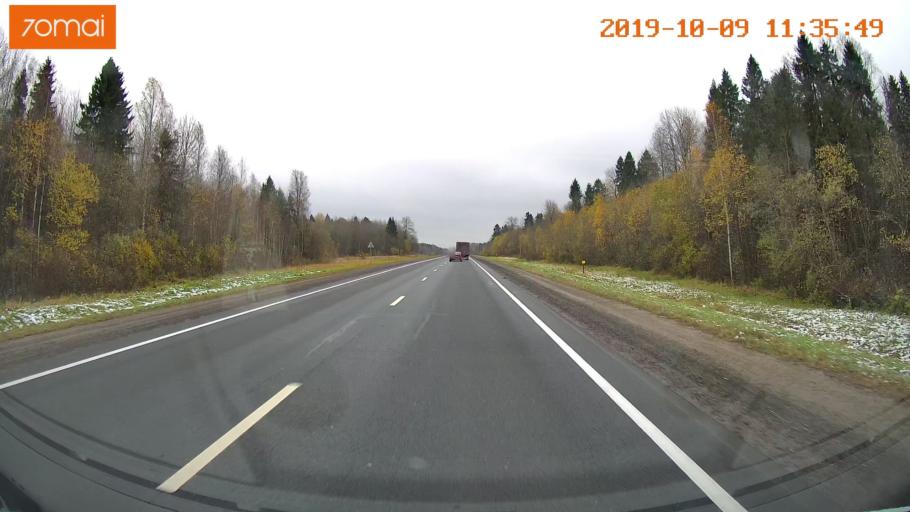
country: RU
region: Vologda
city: Gryazovets
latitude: 58.9986
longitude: 40.1300
